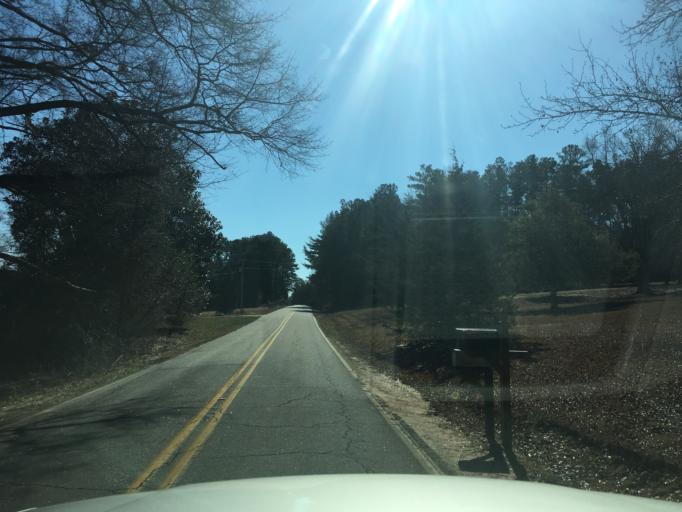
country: US
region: South Carolina
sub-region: Pickens County
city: Pickens
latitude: 34.8308
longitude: -82.7864
